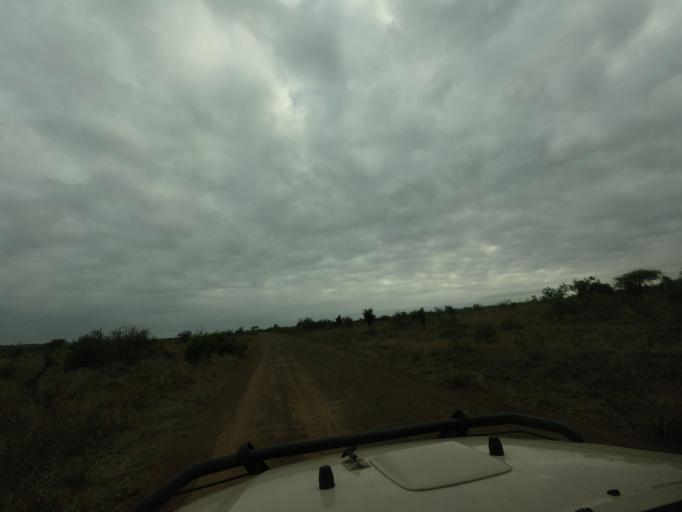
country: ZA
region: Mpumalanga
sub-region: Ehlanzeni District
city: Komatipoort
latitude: -25.3201
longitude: 31.9076
